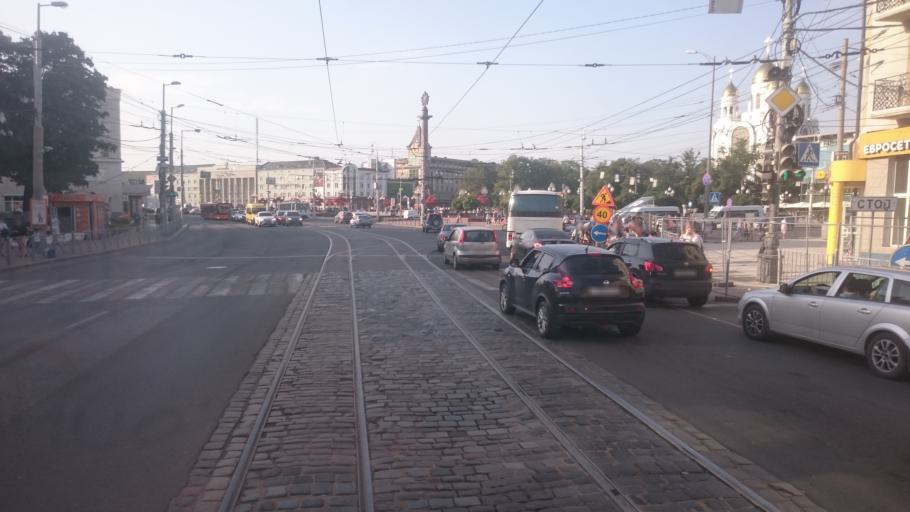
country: RU
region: Kaliningrad
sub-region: Gorod Kaliningrad
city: Kaliningrad
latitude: 54.7184
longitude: 20.5018
